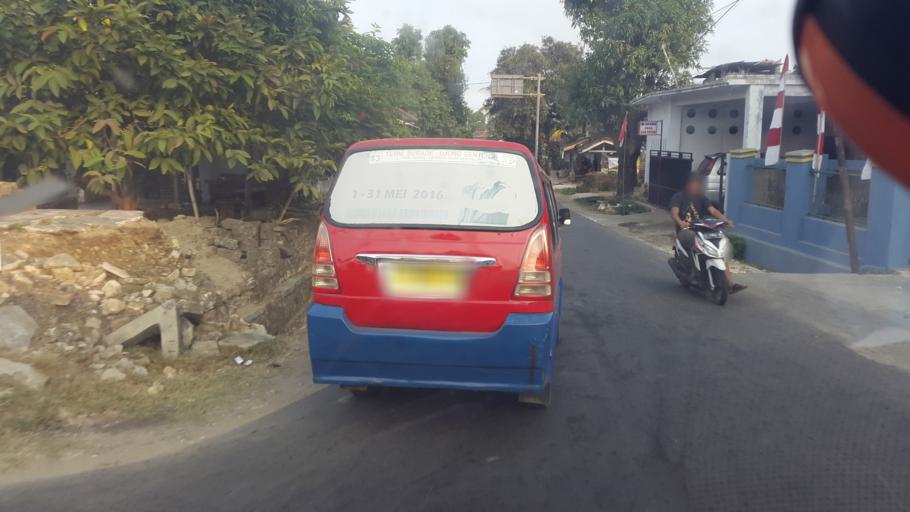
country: ID
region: West Java
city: Pondokaso
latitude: -7.3563
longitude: 106.5434
